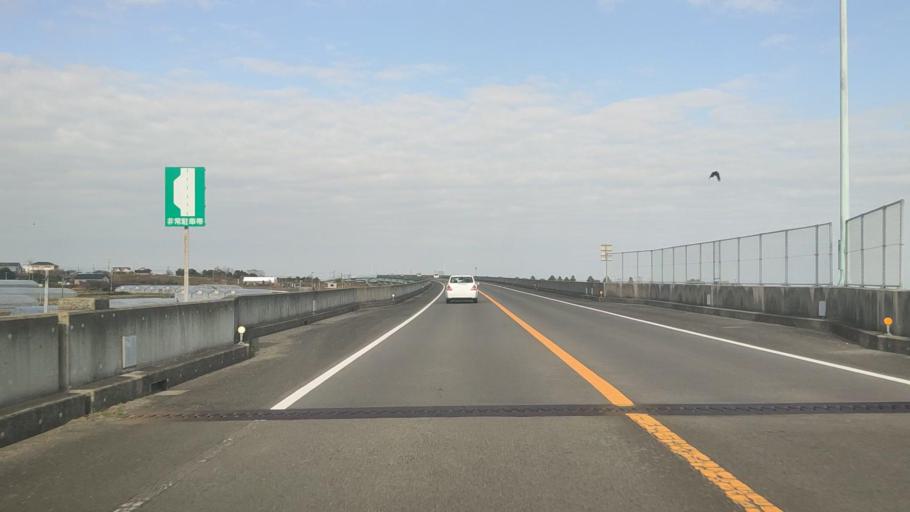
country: JP
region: Nagasaki
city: Shimabara
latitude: 32.7347
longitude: 130.3691
